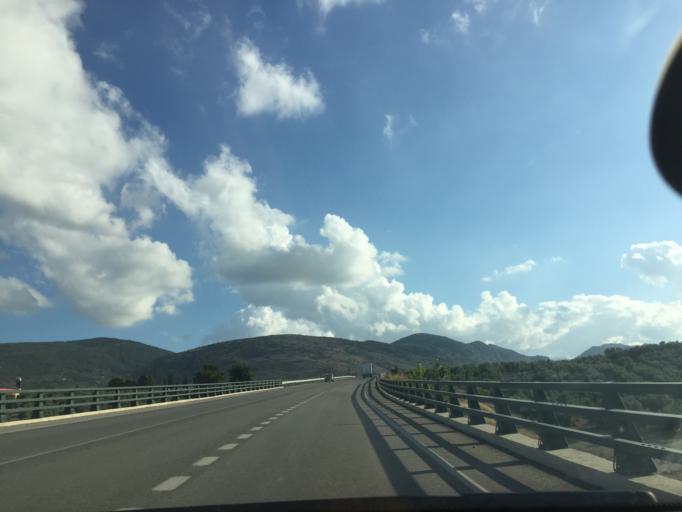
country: ES
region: Andalusia
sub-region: Provincia de Jaen
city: Mancha Real
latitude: 37.7933
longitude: -3.6223
